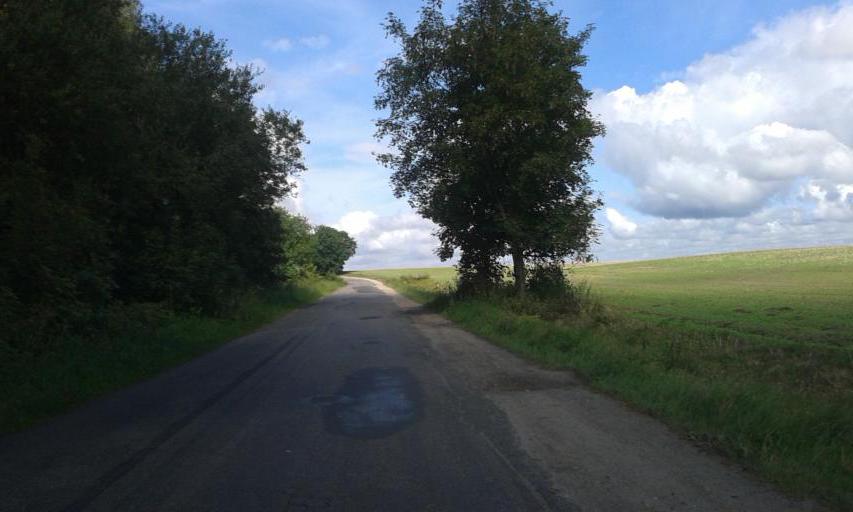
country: PL
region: West Pomeranian Voivodeship
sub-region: Powiat slawienski
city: Slawno
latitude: 54.2966
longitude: 16.6439
